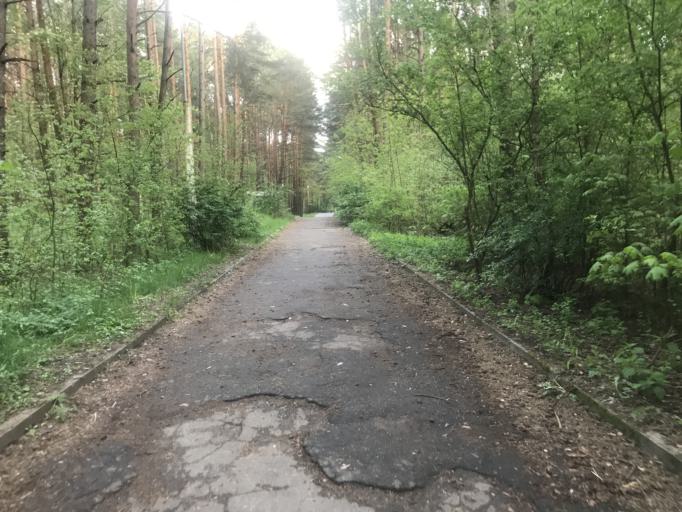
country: BY
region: Minsk
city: Zhdanovichy
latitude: 53.9533
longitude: 27.4253
